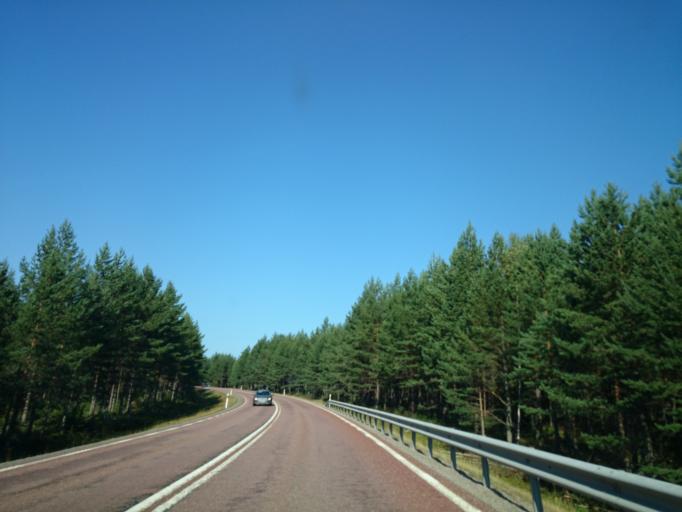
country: SE
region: Gaevleborg
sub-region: Hudiksvalls Kommun
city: Delsbo
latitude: 61.7869
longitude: 16.6293
